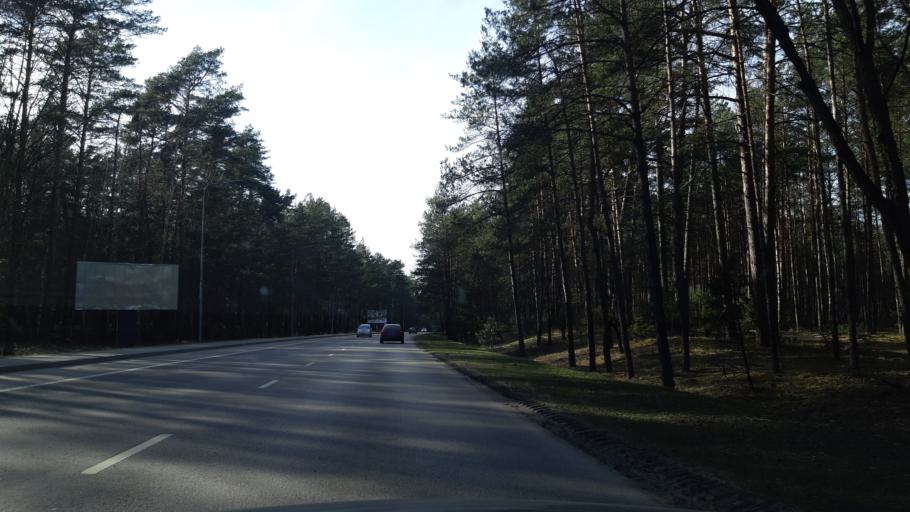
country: LT
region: Alytaus apskritis
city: Druskininkai
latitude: 54.0053
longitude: 24.0077
